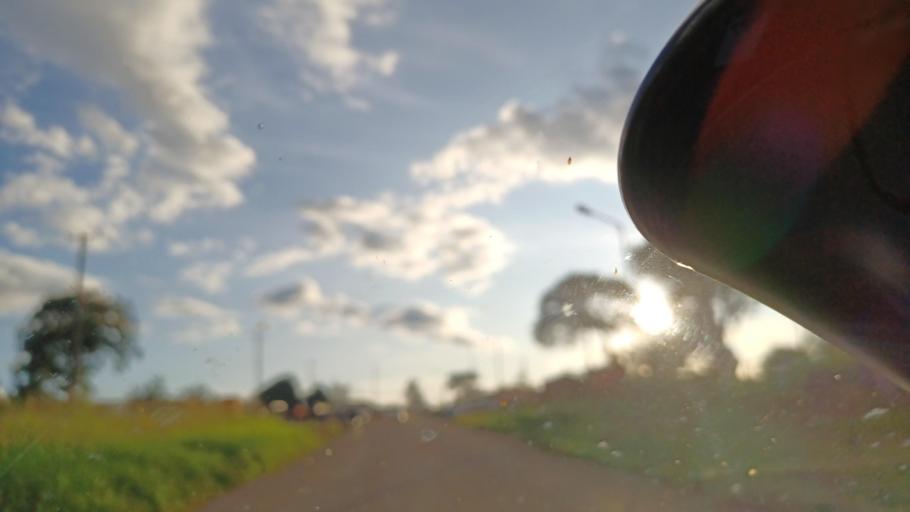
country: ZM
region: North-Western
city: Kasempa
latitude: -13.4583
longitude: 25.8425
